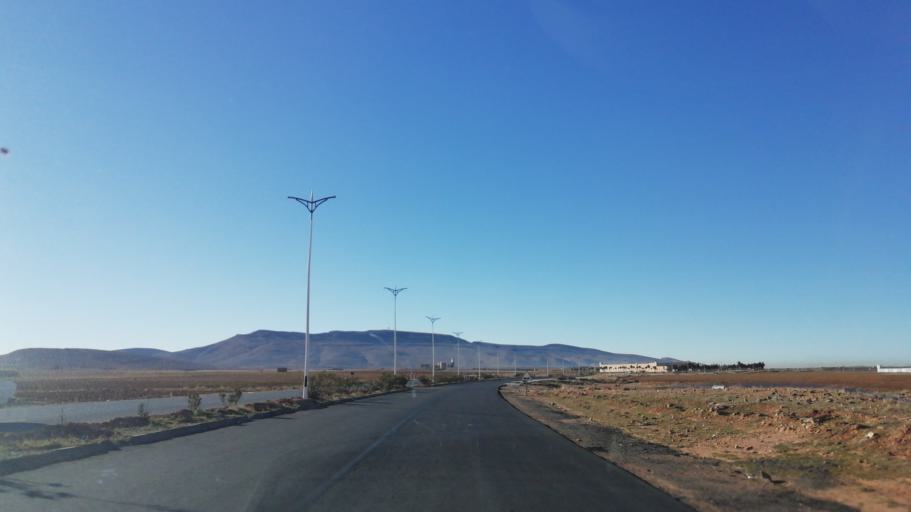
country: DZ
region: El Bayadh
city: El Bayadh
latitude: 33.6961
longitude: 1.0809
